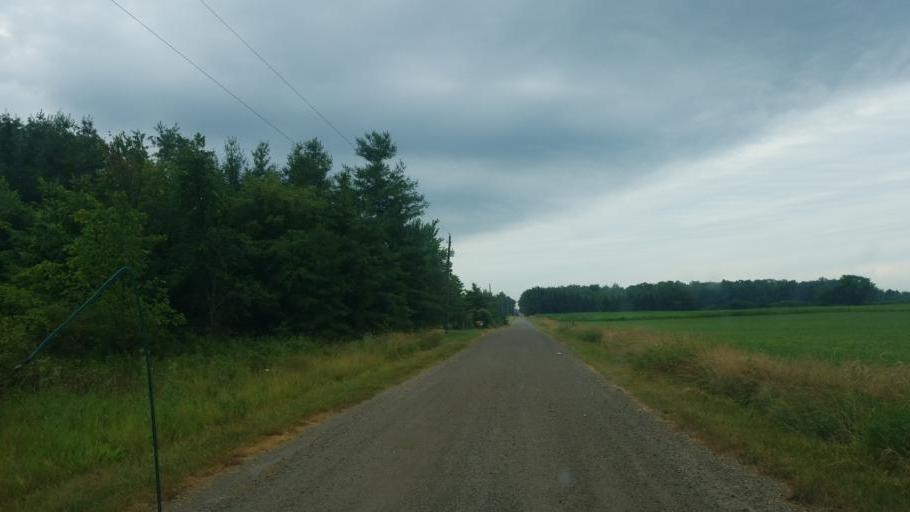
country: US
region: Indiana
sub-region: Steuben County
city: Hamilton
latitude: 41.4859
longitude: -84.9107
